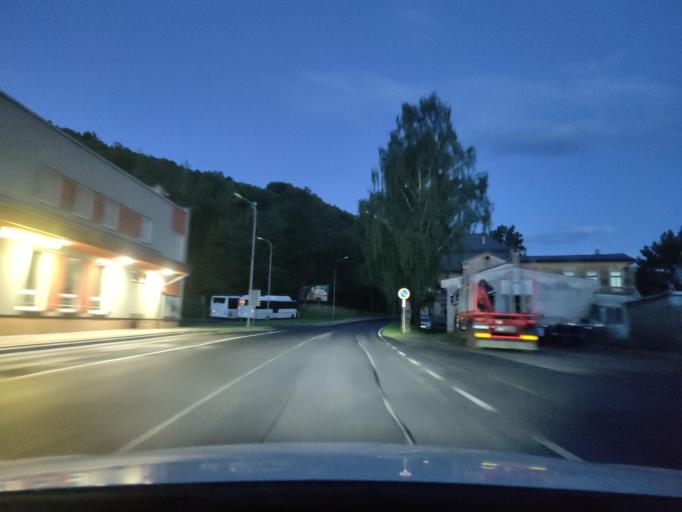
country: CZ
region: Olomoucky
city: Zlate Hory
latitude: 50.2606
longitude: 17.3979
